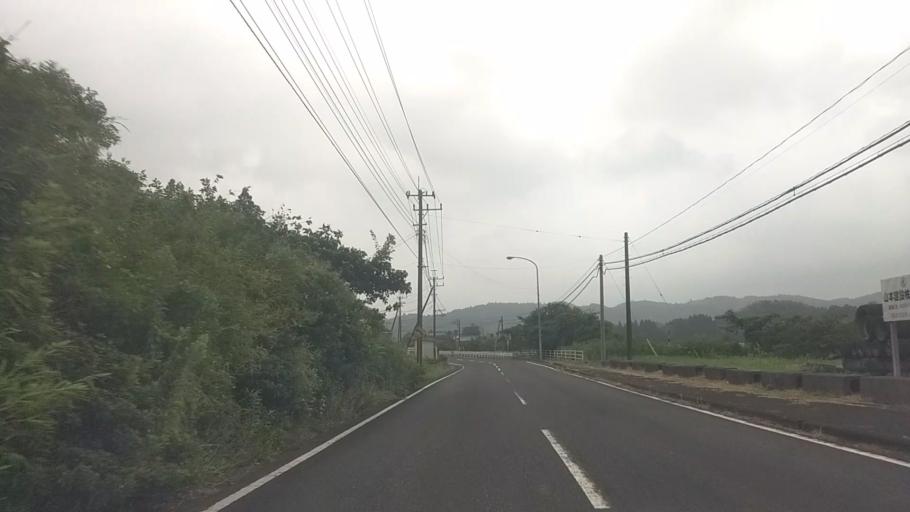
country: JP
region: Chiba
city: Katsuura
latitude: 35.2599
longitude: 140.2482
